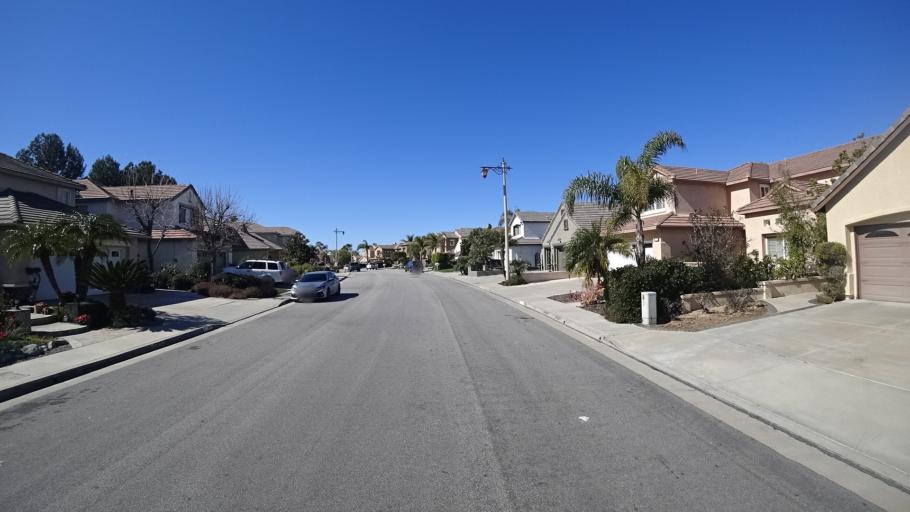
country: US
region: California
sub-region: Orange County
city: Yorba Linda
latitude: 33.8587
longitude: -117.7226
